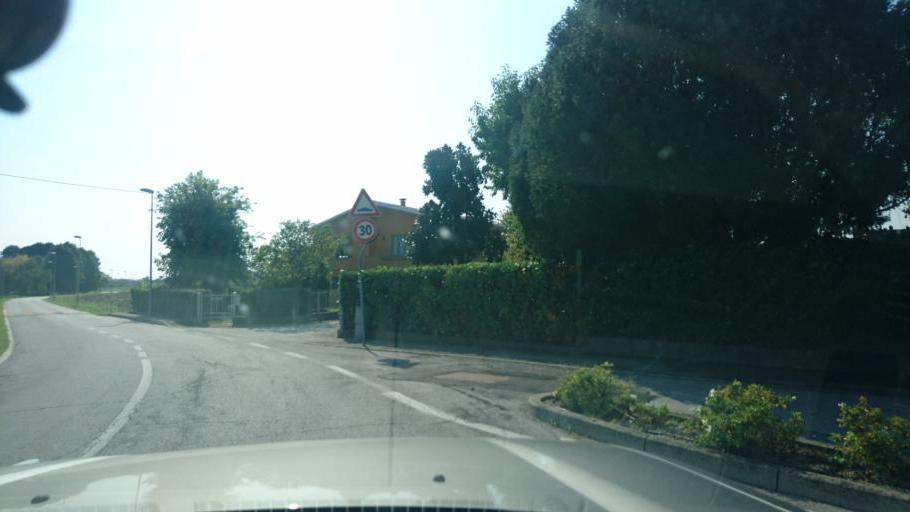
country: IT
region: Veneto
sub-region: Provincia di Padova
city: Casalserugo
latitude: 45.3037
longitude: 11.9022
